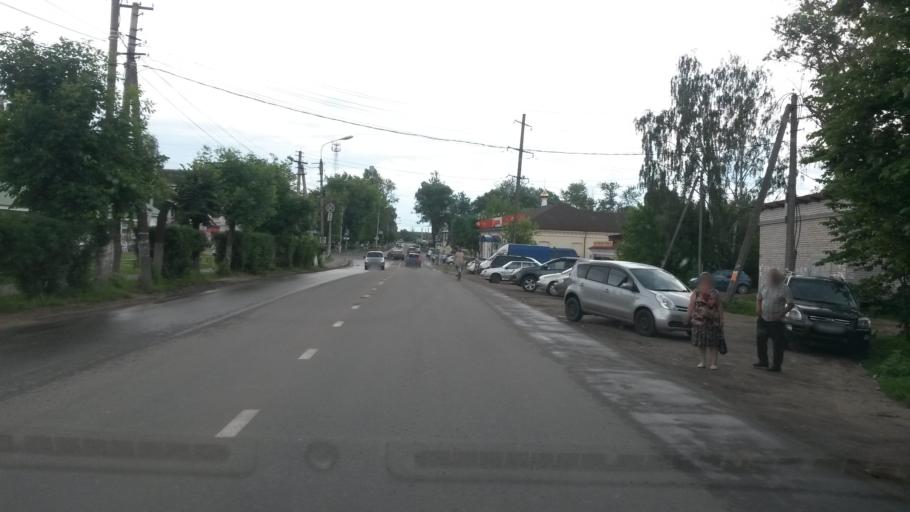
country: RU
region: Jaroslavl
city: Gavrilov-Yam
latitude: 57.3059
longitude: 39.8529
